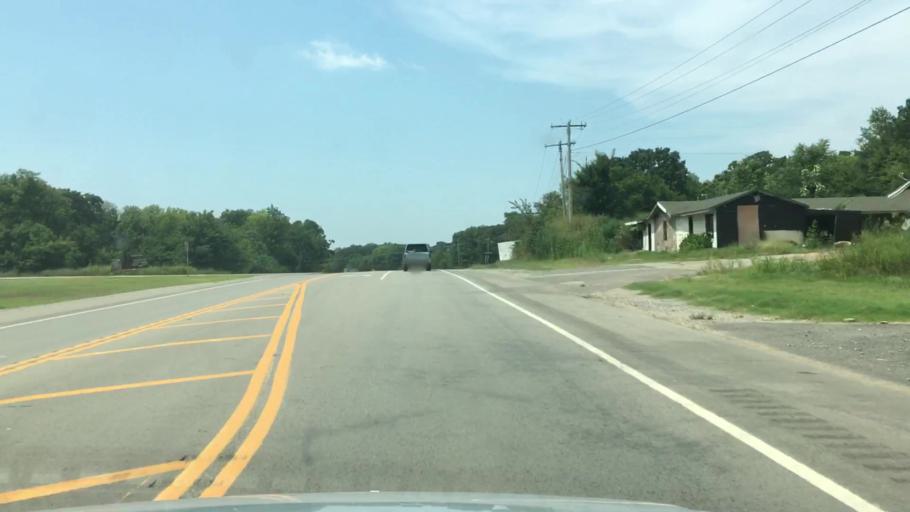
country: US
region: Oklahoma
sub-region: Wagoner County
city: Wagoner
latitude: 35.9297
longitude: -95.2494
